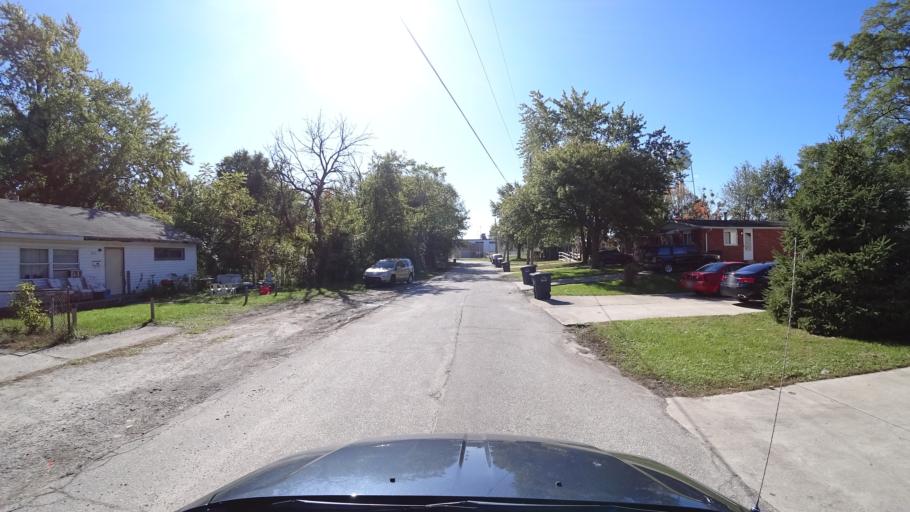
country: US
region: Indiana
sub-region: LaPorte County
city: Michigan City
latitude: 41.7072
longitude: -86.9156
